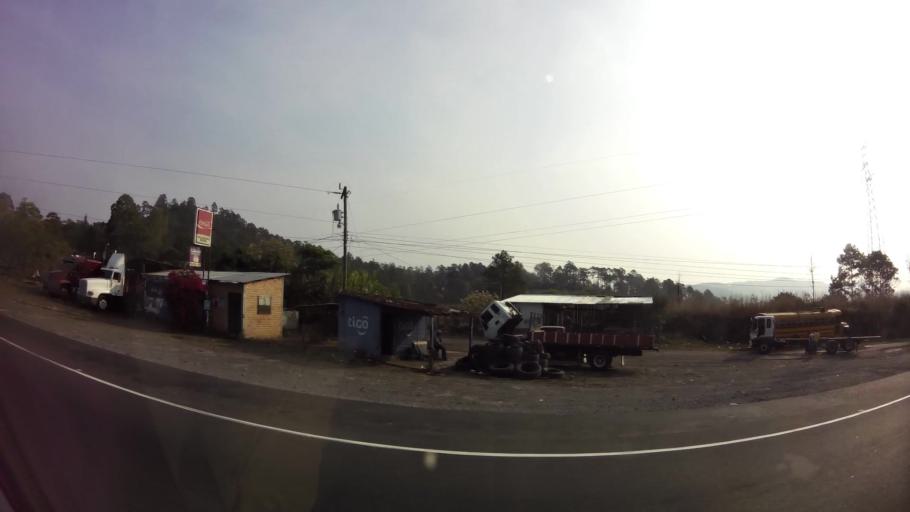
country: HN
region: Francisco Morazan
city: Zambrano
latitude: 14.2659
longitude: -87.3968
